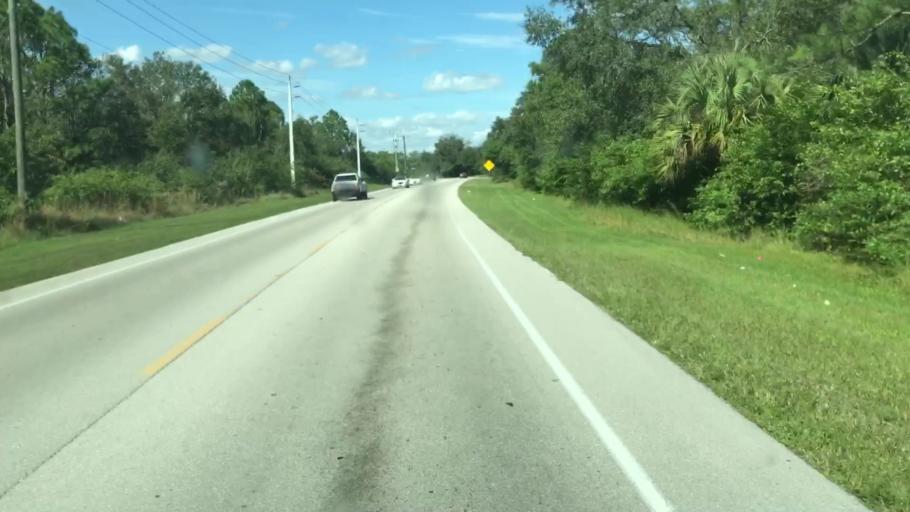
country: US
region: Florida
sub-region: Lee County
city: Alva
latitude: 26.6959
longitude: -81.6007
